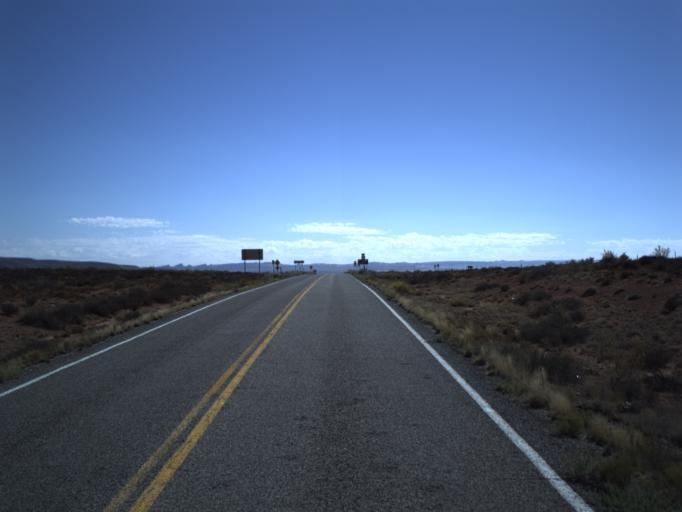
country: US
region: Utah
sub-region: San Juan County
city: Blanding
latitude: 37.2015
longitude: -109.8804
